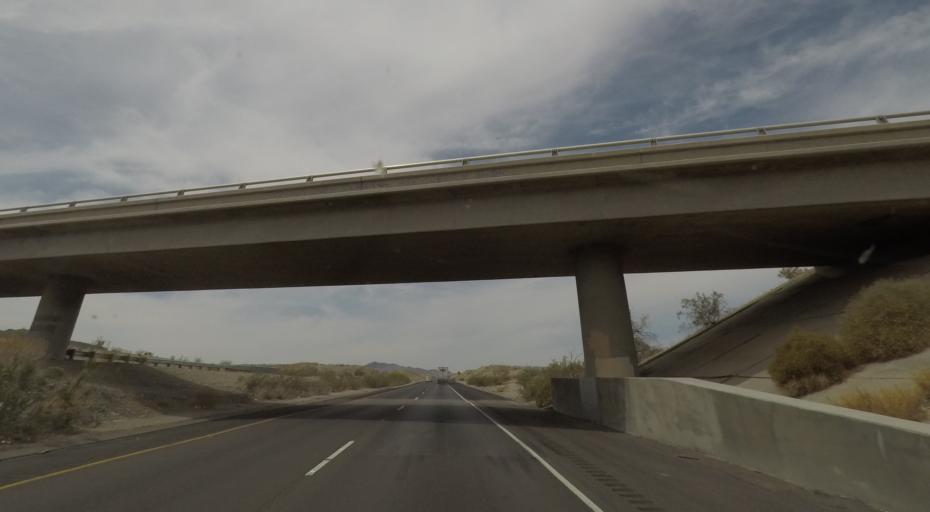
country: US
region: California
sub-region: San Bernardino County
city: Needles
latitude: 34.7177
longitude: -114.5106
